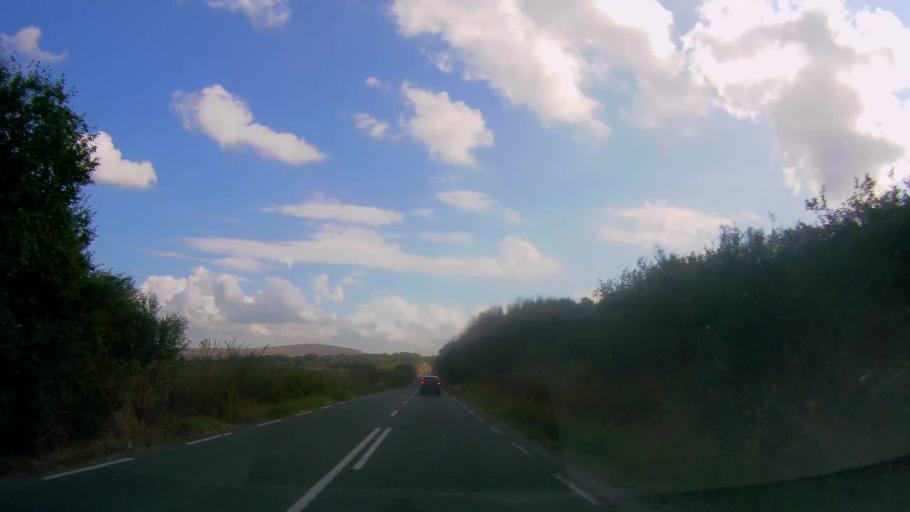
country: BG
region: Burgas
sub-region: Obshtina Kameno
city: Kameno
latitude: 42.4875
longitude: 27.3404
